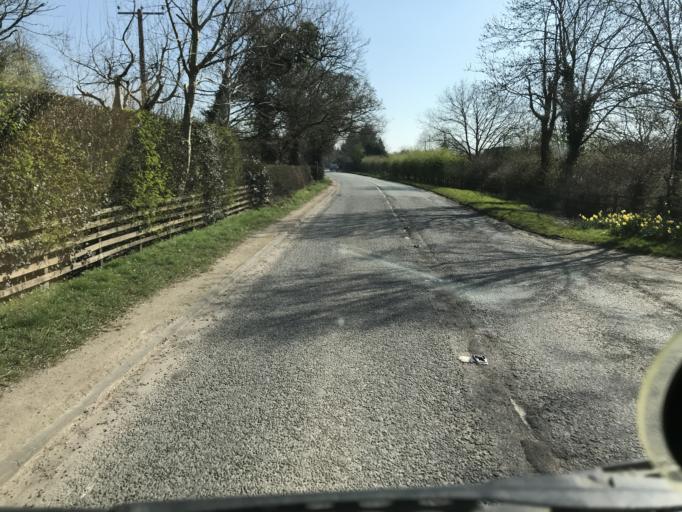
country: GB
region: England
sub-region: Cheshire East
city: Mobberley
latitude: 53.2819
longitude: -2.3150
